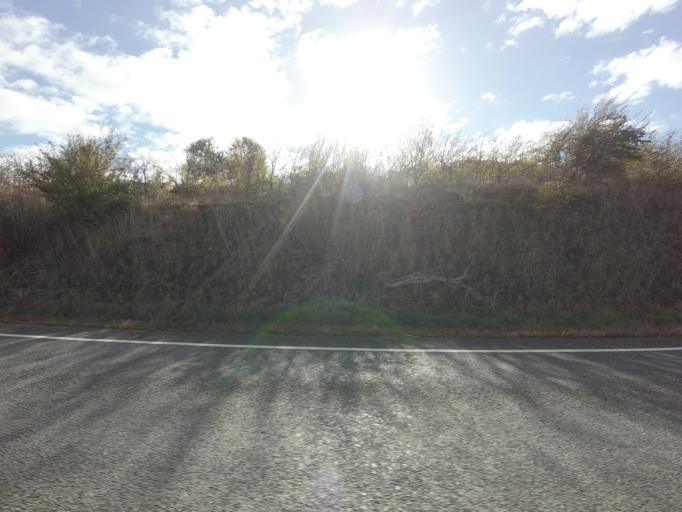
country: AU
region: Tasmania
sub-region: Derwent Valley
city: New Norfolk
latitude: -42.7238
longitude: 146.9514
